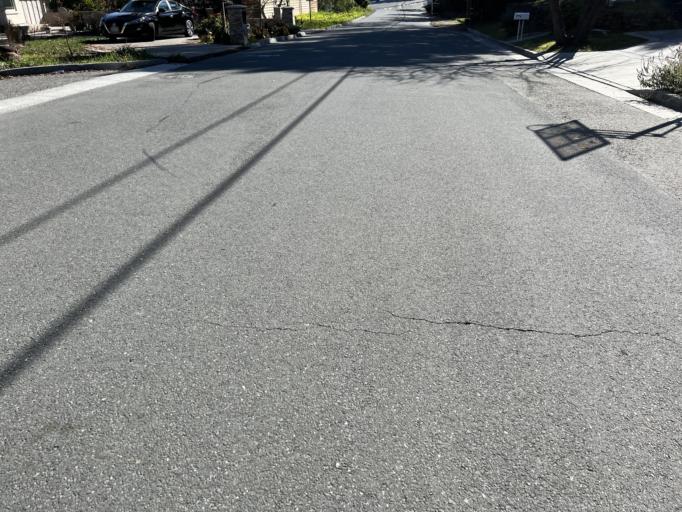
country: US
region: California
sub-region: Santa Clara County
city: Cupertino
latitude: 37.3125
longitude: -122.0700
